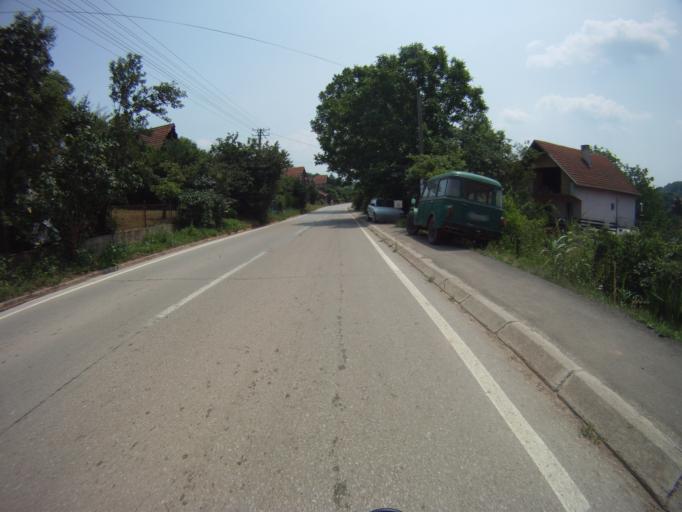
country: RS
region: Central Serbia
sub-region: Nisavski Okrug
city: Gadzin Han
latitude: 43.2394
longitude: 22.0170
